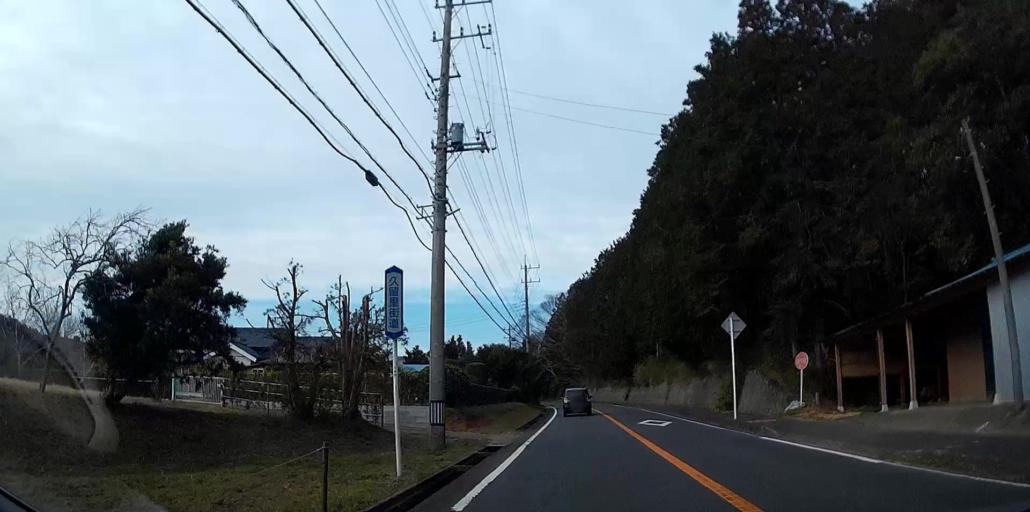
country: JP
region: Chiba
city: Kawaguchi
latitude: 35.2641
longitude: 140.0581
